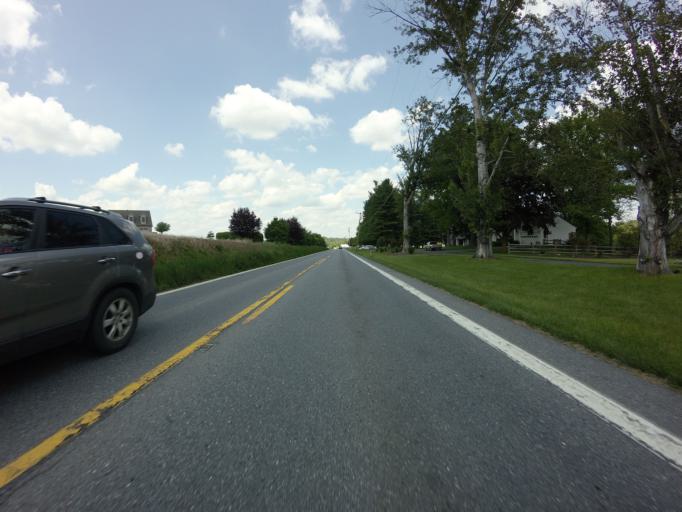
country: US
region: Maryland
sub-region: Frederick County
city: Green Valley
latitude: 39.2975
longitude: -77.3052
